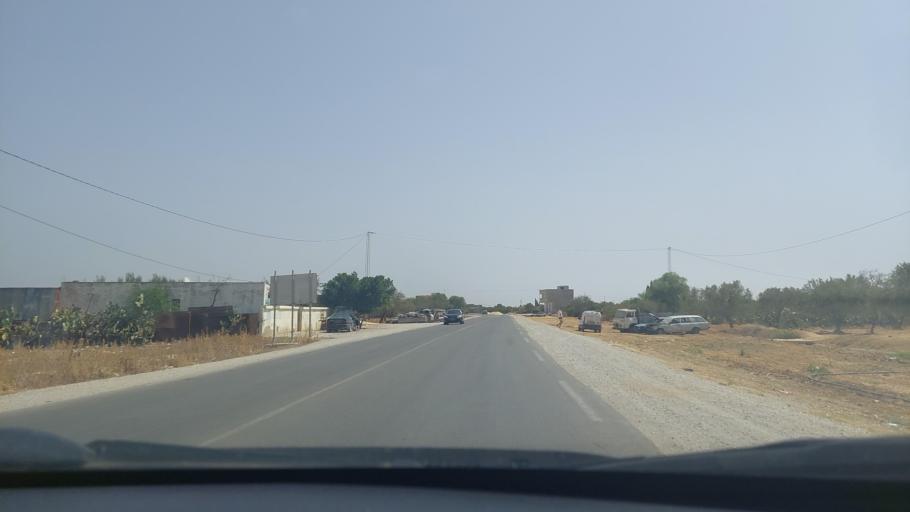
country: TN
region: Al Munastir
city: Qasr Hallal
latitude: 35.6032
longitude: 10.8934
